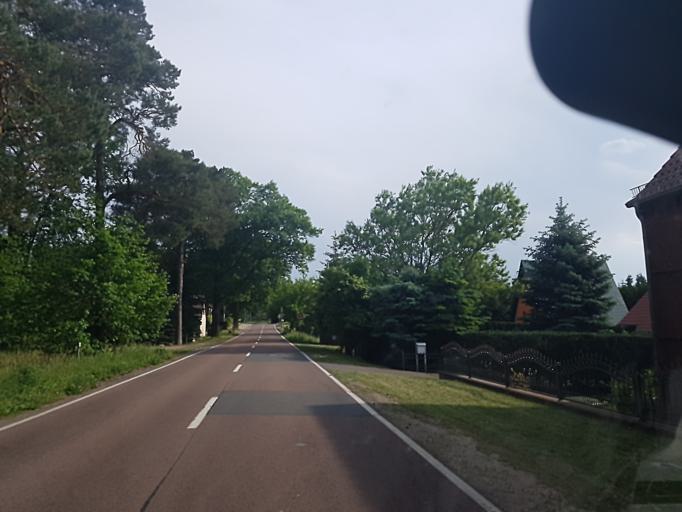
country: DE
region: Saxony-Anhalt
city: Nudersdorf
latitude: 51.9320
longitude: 12.6018
